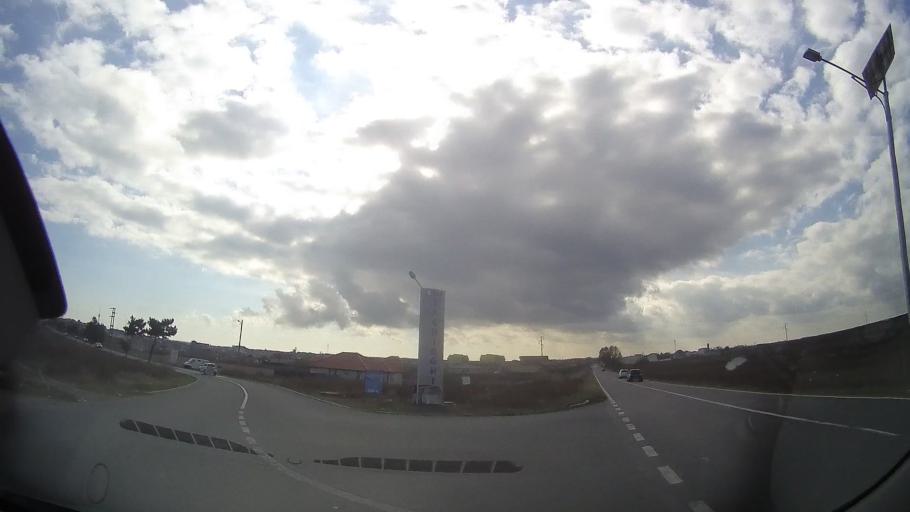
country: RO
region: Constanta
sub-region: Oras Techirghiol
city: Techirghiol
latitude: 44.0657
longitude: 28.5936
